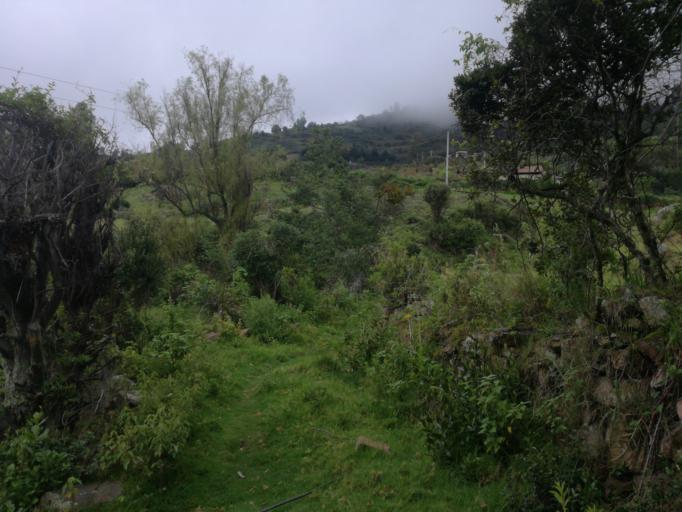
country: CO
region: Boyaca
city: Socha Viejo
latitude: 6.0039
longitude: -72.6833
